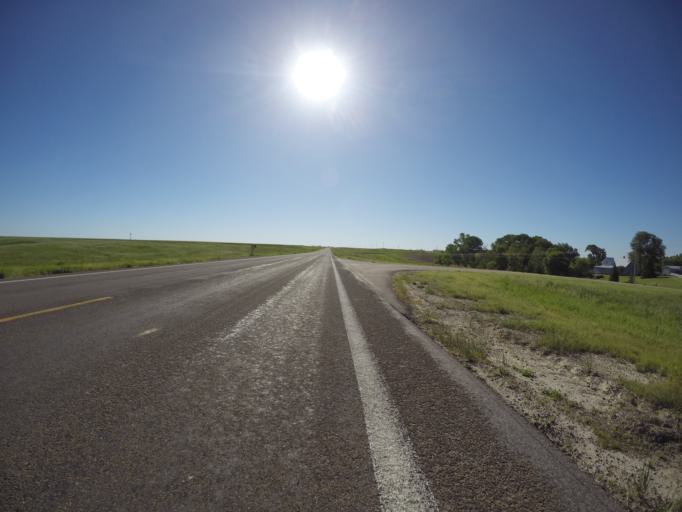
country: US
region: Kansas
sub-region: Norton County
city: Norton
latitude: 39.8280
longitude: -100.0242
